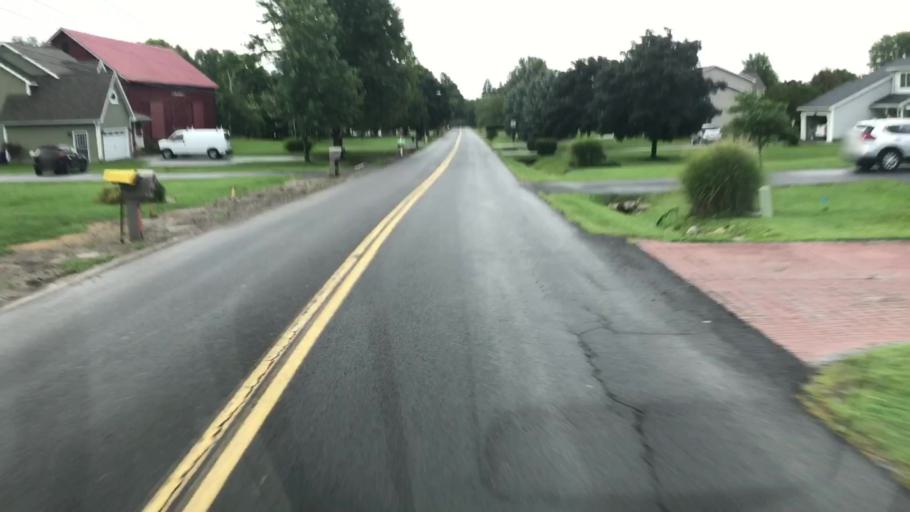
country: US
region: New York
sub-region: Cayuga County
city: Melrose Park
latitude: 42.9120
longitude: -76.5294
